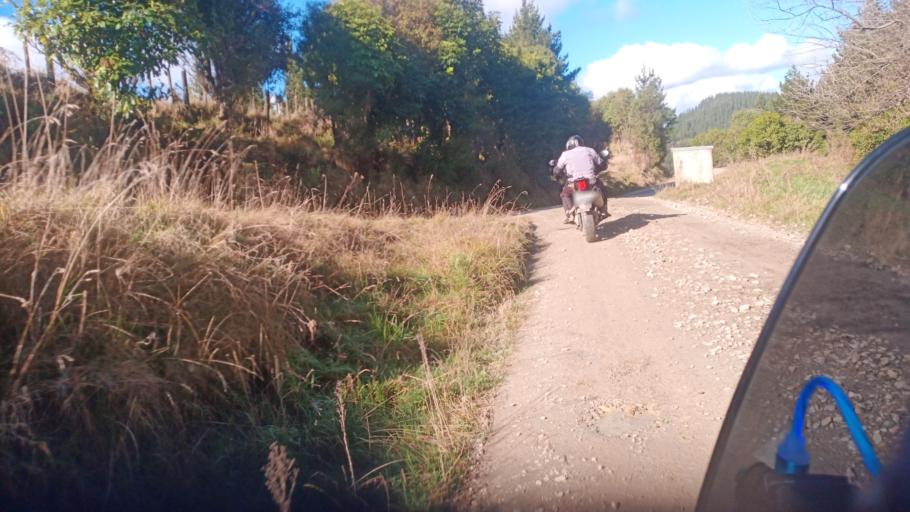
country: NZ
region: Hawke's Bay
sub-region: Wairoa District
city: Wairoa
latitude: -38.6667
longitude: 177.5381
